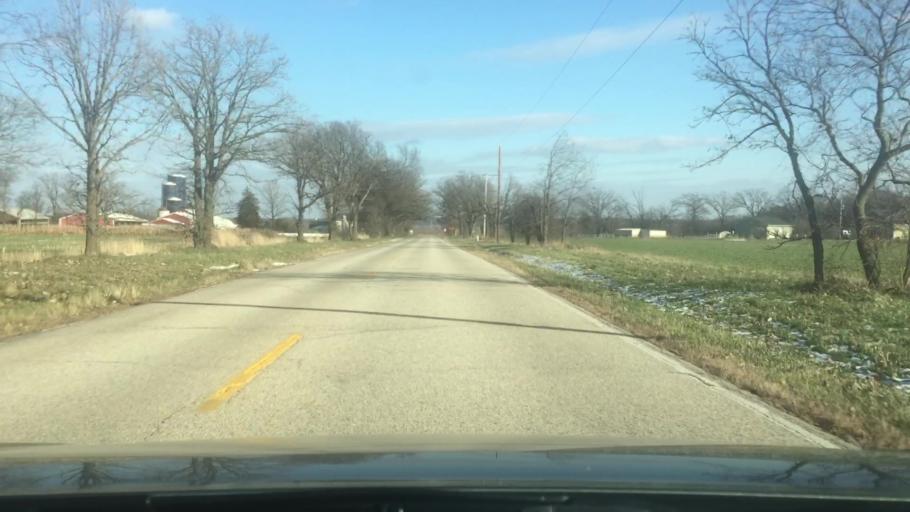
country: US
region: Wisconsin
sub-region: Waukesha County
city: Eagle
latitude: 42.9172
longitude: -88.5256
